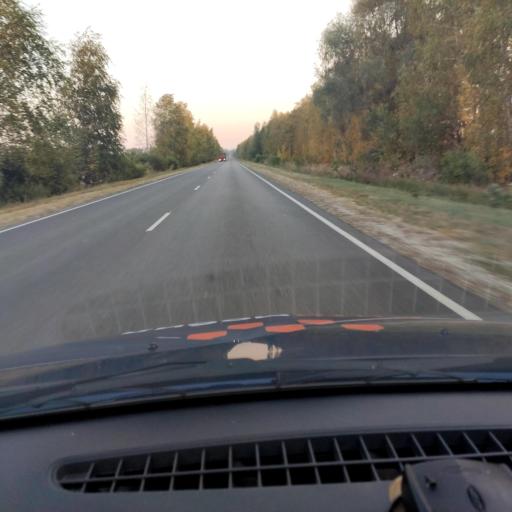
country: RU
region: Voronezj
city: Latnaya
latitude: 51.6347
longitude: 38.7838
